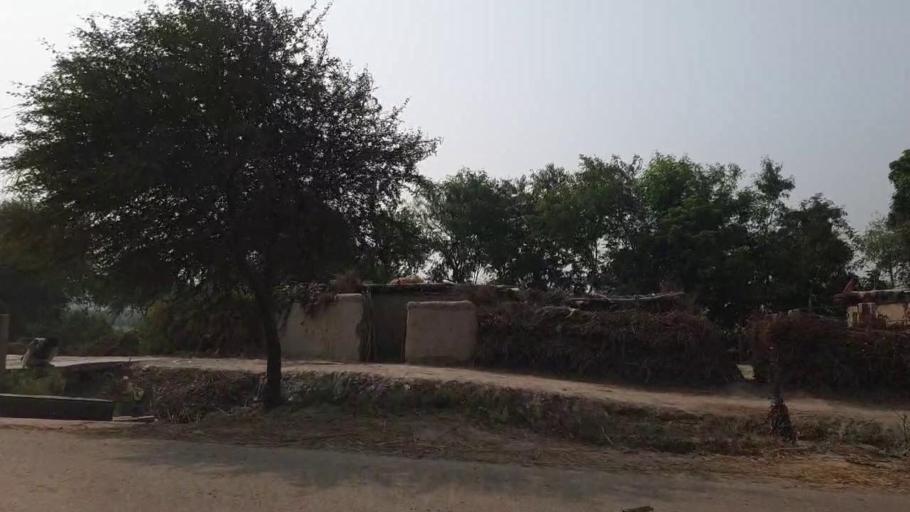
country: PK
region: Sindh
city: Tando Muhammad Khan
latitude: 25.1960
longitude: 68.5736
